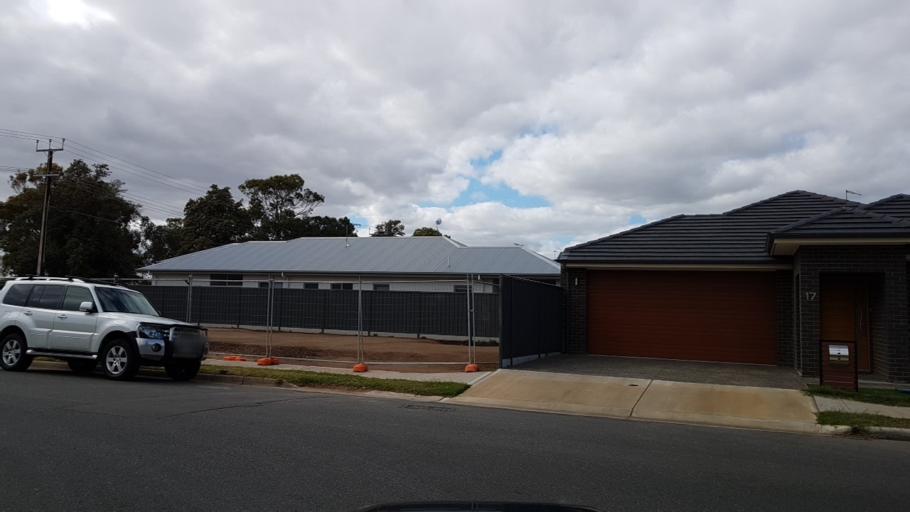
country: AU
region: South Australia
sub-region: Charles Sturt
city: Seaton
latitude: -34.9098
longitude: 138.5206
